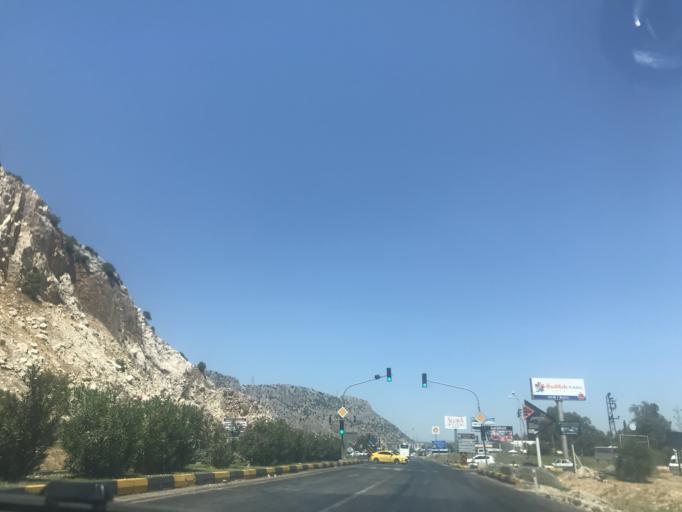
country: TR
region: Antalya
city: Cakirlar
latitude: 36.8304
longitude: 30.5954
